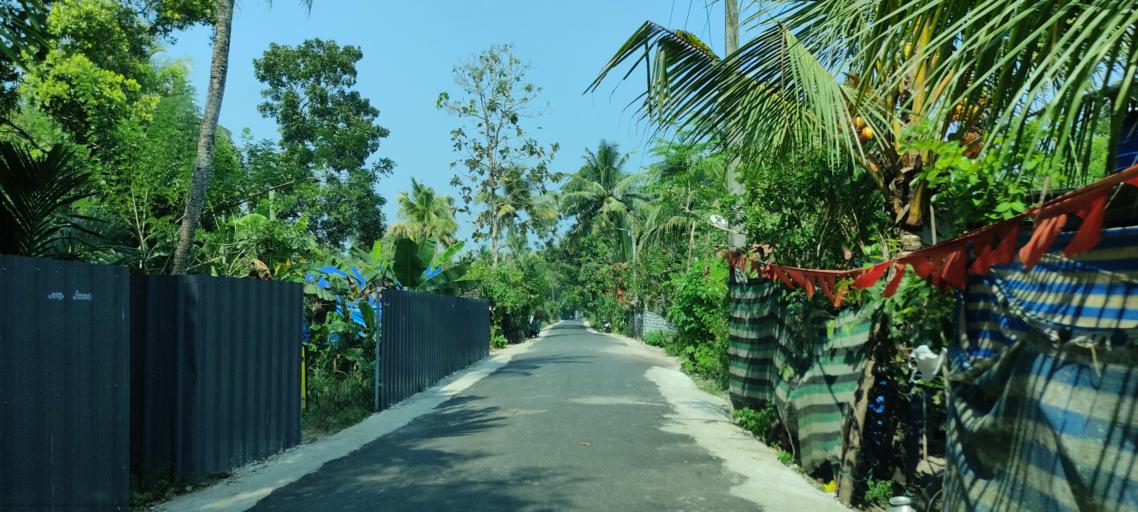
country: IN
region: Kerala
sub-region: Alappuzha
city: Alleppey
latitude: 9.5429
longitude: 76.3204
